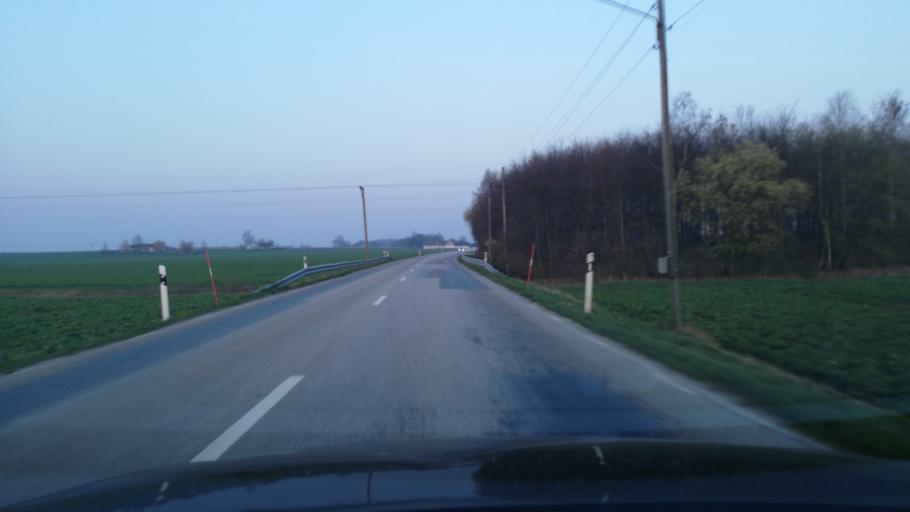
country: SE
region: Skane
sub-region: Tomelilla Kommun
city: Tomelilla
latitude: 55.4953
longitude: 14.1203
